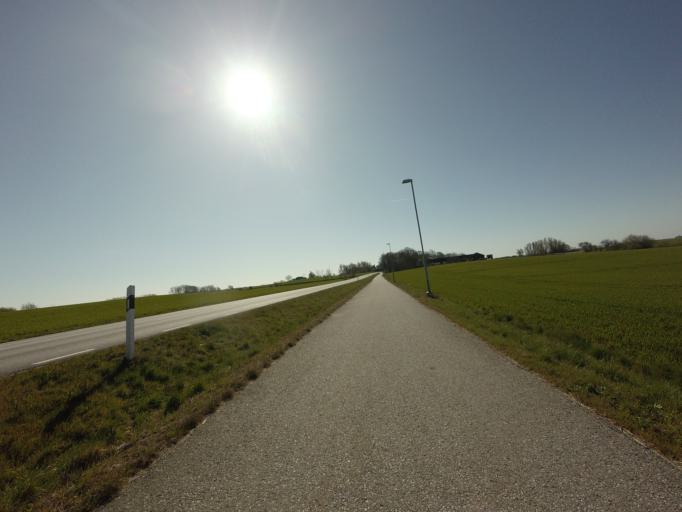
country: SE
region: Skane
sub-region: Malmo
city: Oxie
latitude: 55.4866
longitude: 13.1229
